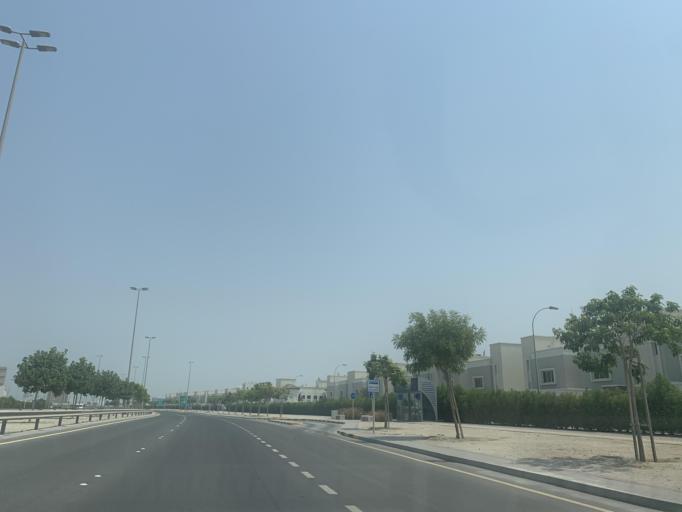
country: BH
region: Muharraq
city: Al Muharraq
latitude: 26.3127
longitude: 50.6277
